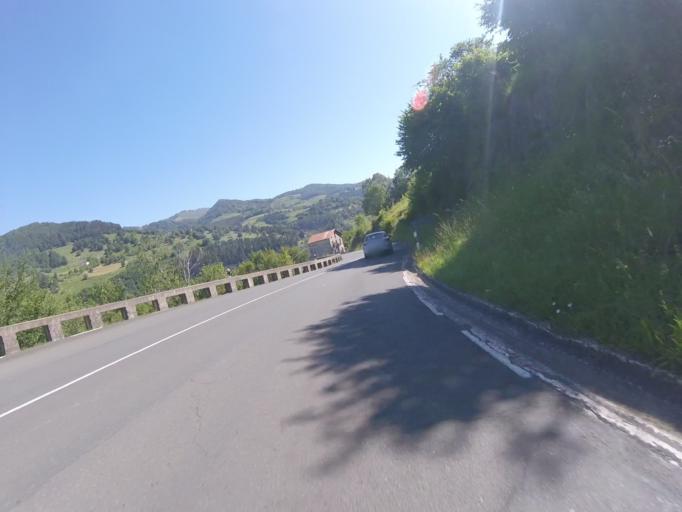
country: ES
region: Basque Country
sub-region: Provincia de Guipuzcoa
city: Albiztur
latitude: 43.1257
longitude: -2.1361
